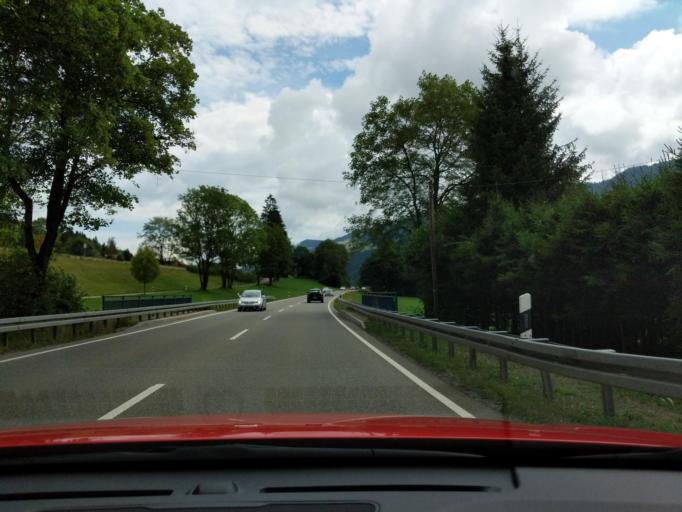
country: DE
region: Bavaria
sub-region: Swabia
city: Oberstaufen
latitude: 47.5548
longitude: 10.0649
